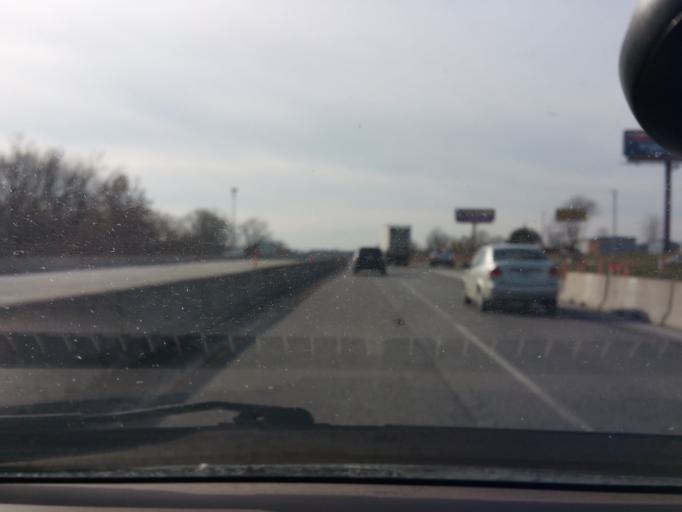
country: US
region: Missouri
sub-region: Clay County
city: Pleasant Valley
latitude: 39.2132
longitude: -94.4788
